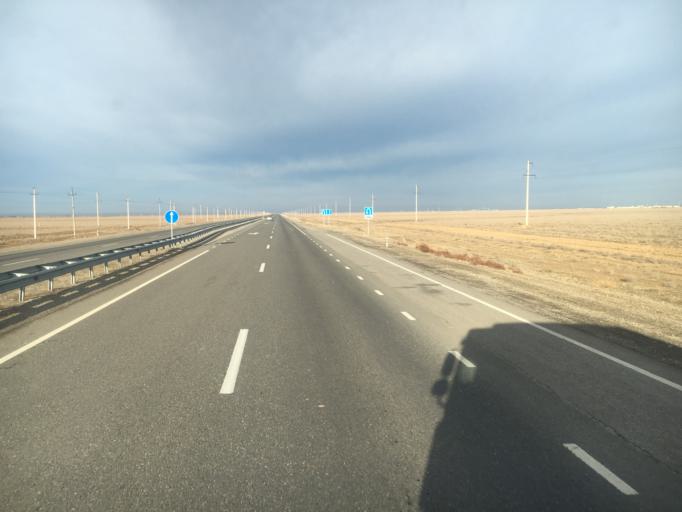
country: KZ
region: Ongtustik Qazaqstan
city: Turkestan
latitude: 43.4284
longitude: 67.9960
